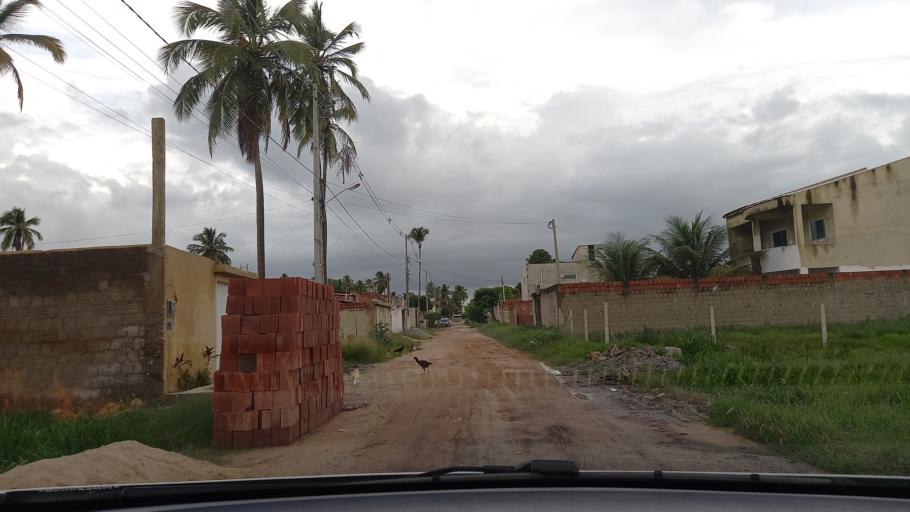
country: BR
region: Pernambuco
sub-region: Sao Jose Da Coroa Grande
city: Sao Jose da Coroa Grande
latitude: -8.9226
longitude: -35.1613
